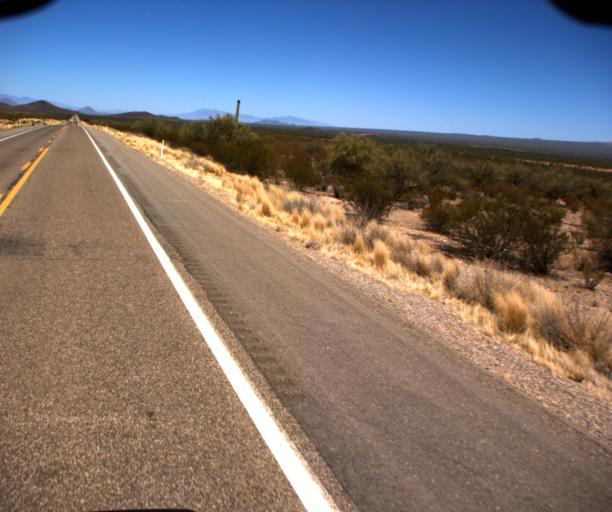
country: US
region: Arizona
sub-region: Pima County
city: Three Points
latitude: 32.0436
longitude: -111.4378
